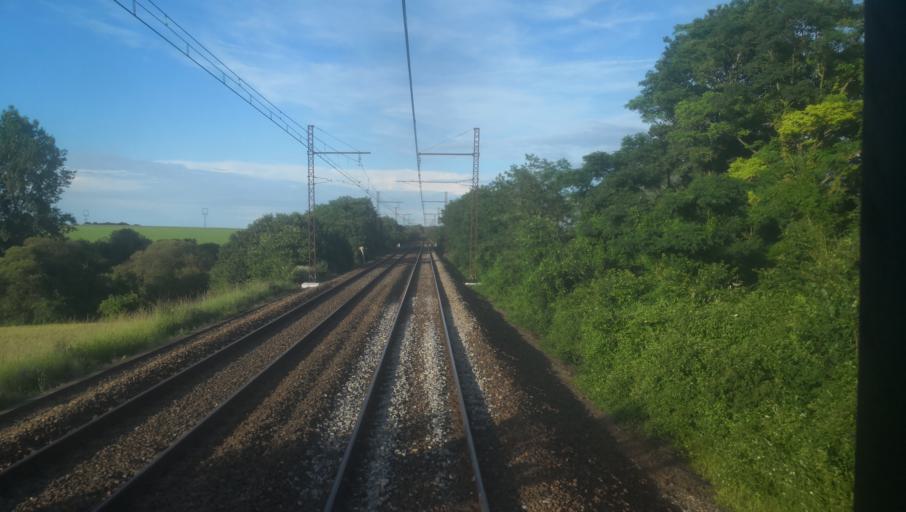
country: FR
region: Centre
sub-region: Departement de l'Indre
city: Neuvy-Pailloux
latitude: 46.8934
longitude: 1.8852
